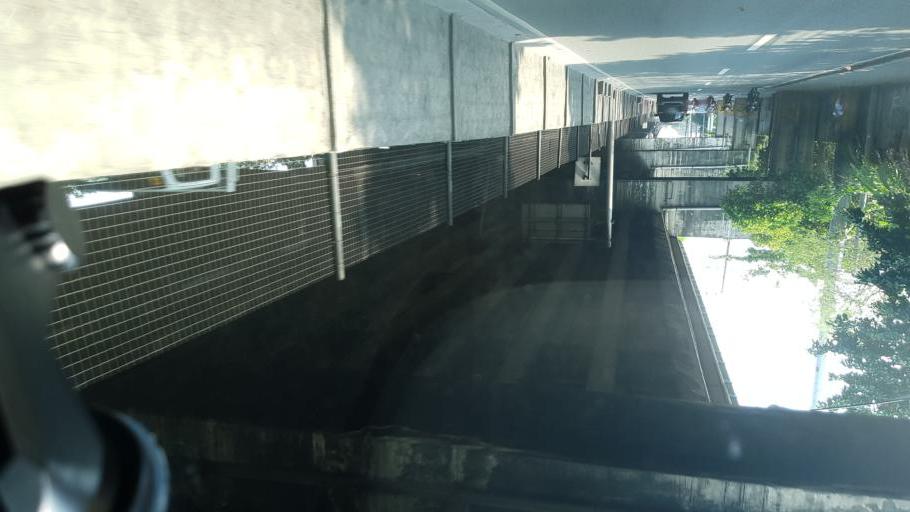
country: PH
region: Calabarzon
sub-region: Province of Rizal
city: Taguig
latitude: 14.4917
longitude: 121.0427
